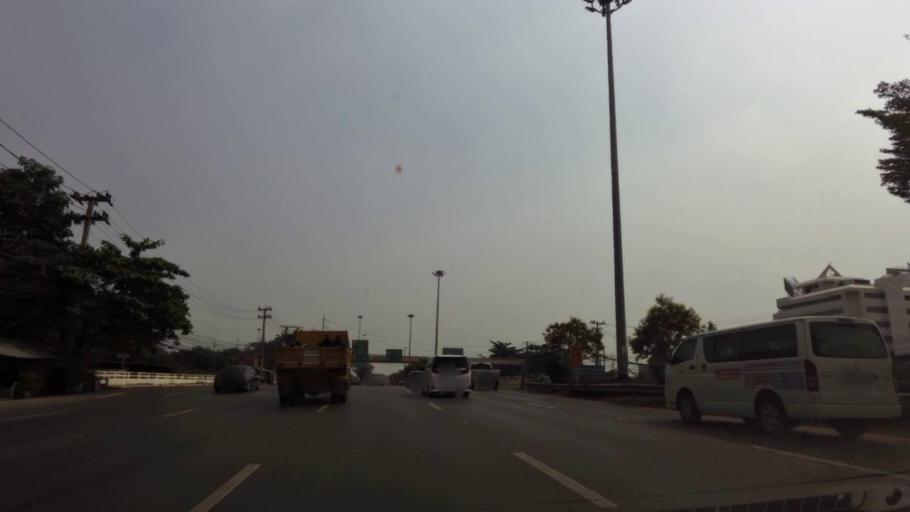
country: TH
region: Phra Nakhon Si Ayutthaya
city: Phra Nakhon Si Ayutthaya
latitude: 14.3442
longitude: 100.6093
